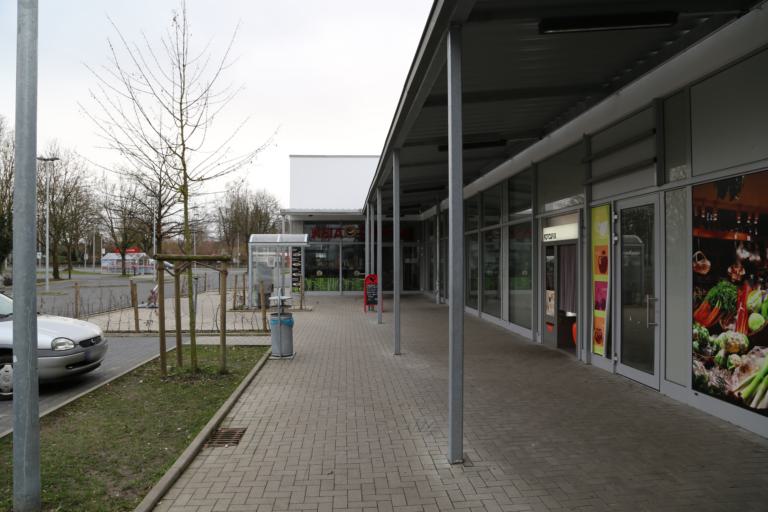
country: DE
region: North Rhine-Westphalia
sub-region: Regierungsbezirk Detmold
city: Lage
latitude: 51.9906
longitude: 8.7912
